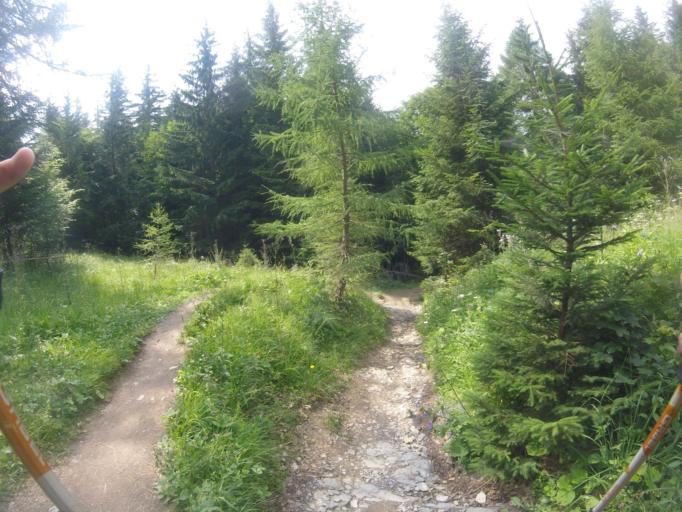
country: SK
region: Zilinsky
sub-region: Okres Zilina
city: Terchova
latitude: 49.2295
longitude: 19.0840
